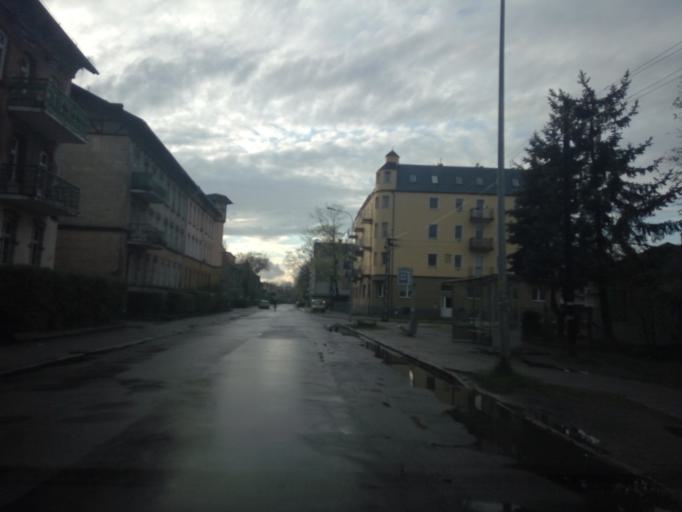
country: PL
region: Lower Silesian Voivodeship
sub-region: Powiat wroclawski
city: Radwanice
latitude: 51.0602
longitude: 17.0836
